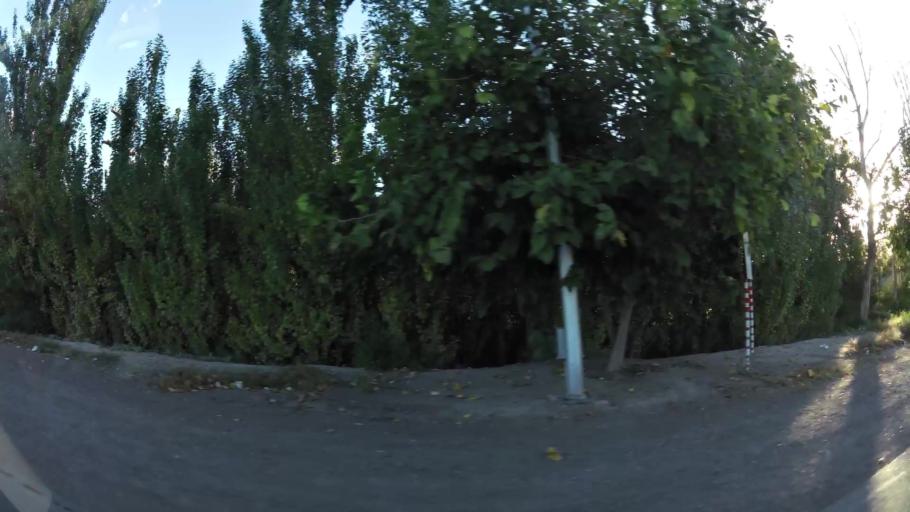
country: AR
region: San Juan
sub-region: Departamento de Santa Lucia
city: Santa Lucia
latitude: -31.5520
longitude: -68.4785
